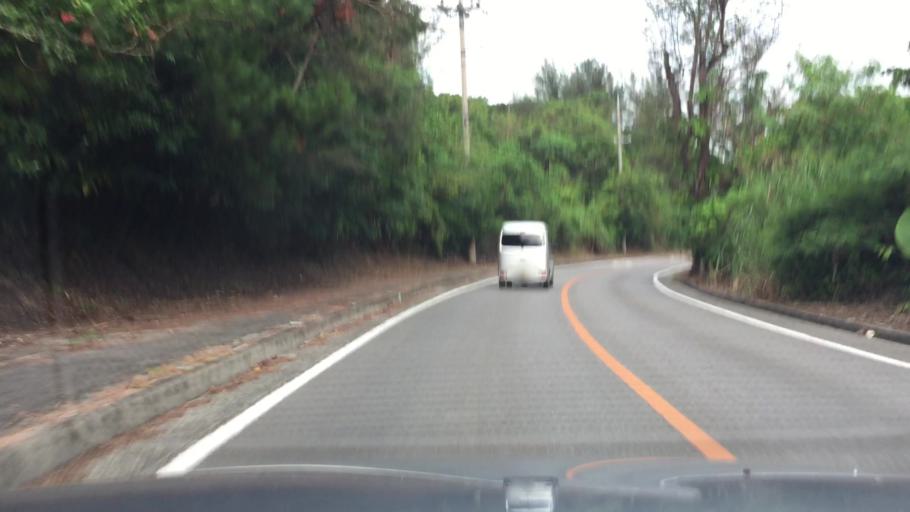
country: JP
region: Okinawa
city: Ishigaki
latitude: 24.4034
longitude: 124.1484
